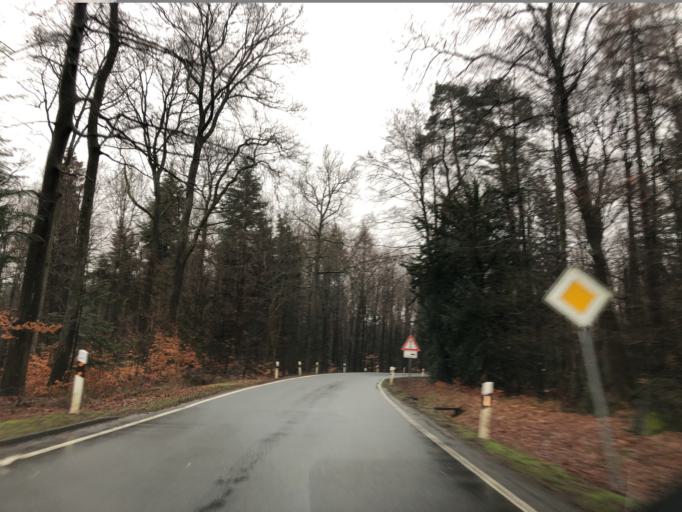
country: DE
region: Hesse
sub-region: Regierungsbezirk Darmstadt
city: Lutzelbach
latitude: 49.7339
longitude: 9.0849
